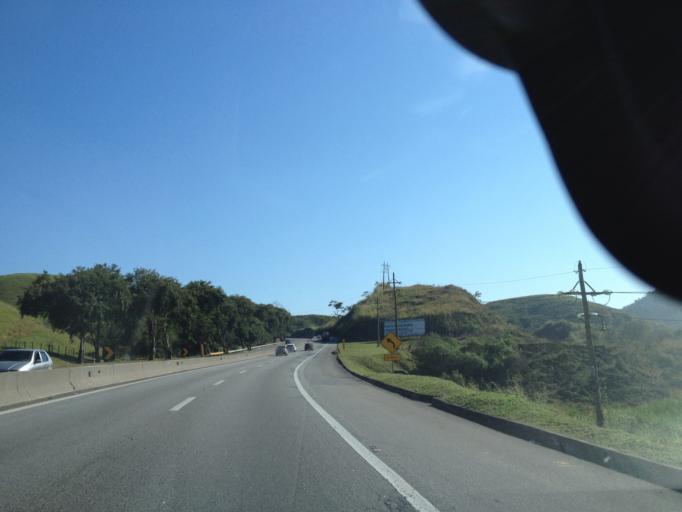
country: BR
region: Rio de Janeiro
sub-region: Porto Real
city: Porto Real
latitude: -22.4811
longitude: -44.2613
